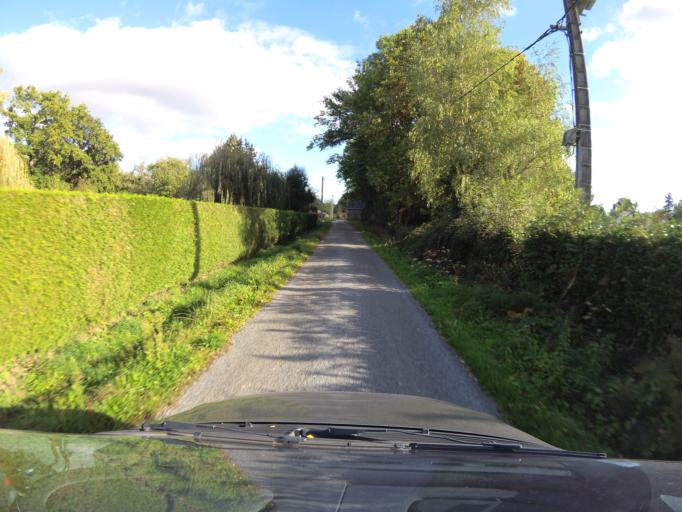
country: FR
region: Brittany
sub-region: Departement du Morbihan
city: Peillac
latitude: 47.7213
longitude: -2.2249
